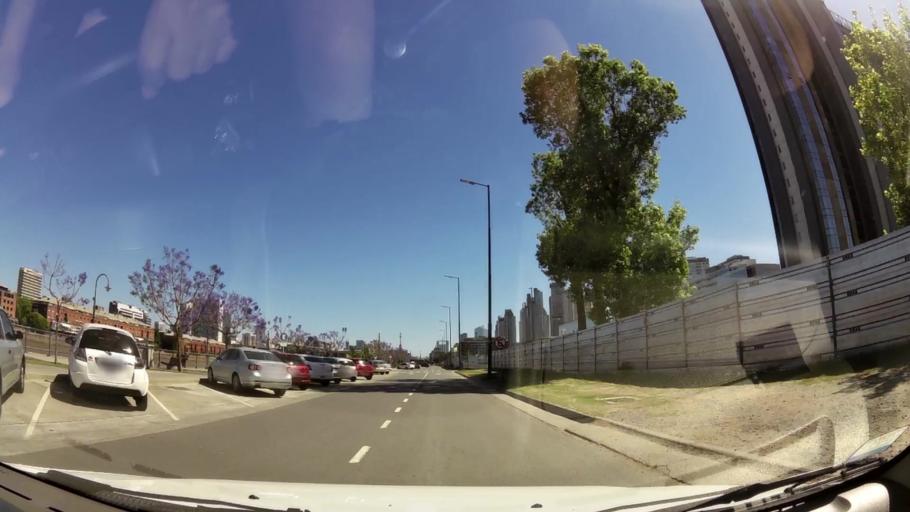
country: AR
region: Buenos Aires F.D.
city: Buenos Aires
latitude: -34.6220
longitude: -58.3625
